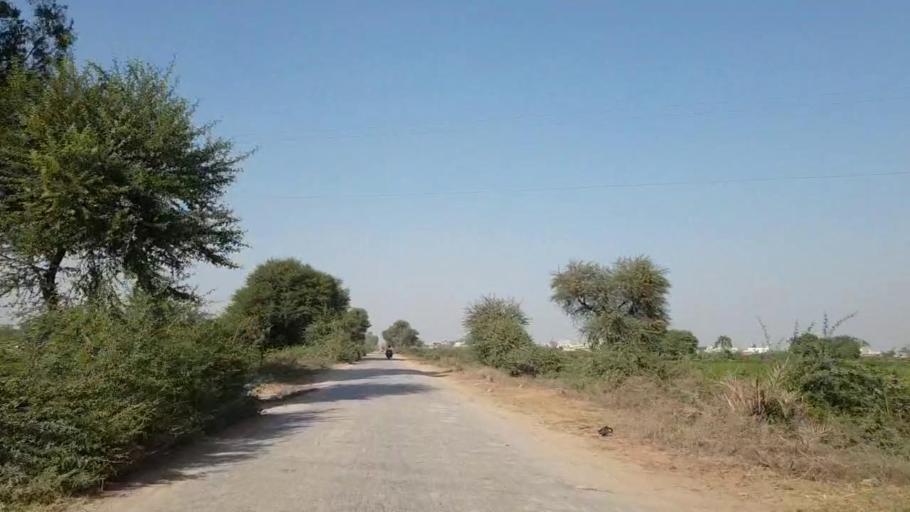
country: PK
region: Sindh
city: Digri
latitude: 25.1416
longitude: 69.1117
